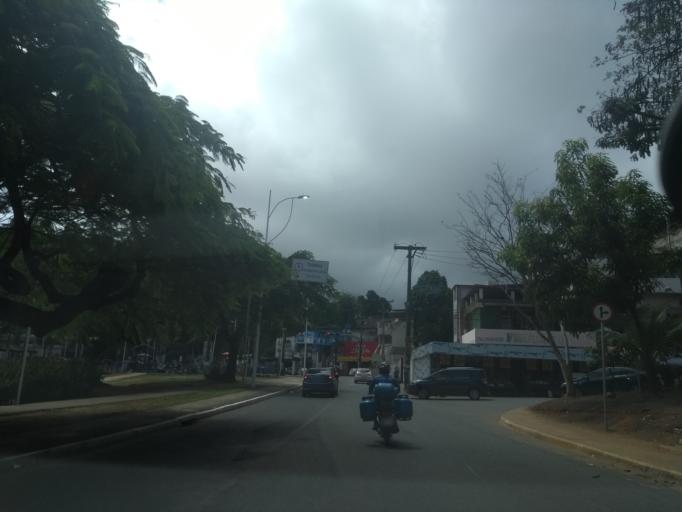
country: BR
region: Bahia
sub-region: Salvador
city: Salvador
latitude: -13.0009
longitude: -38.5182
